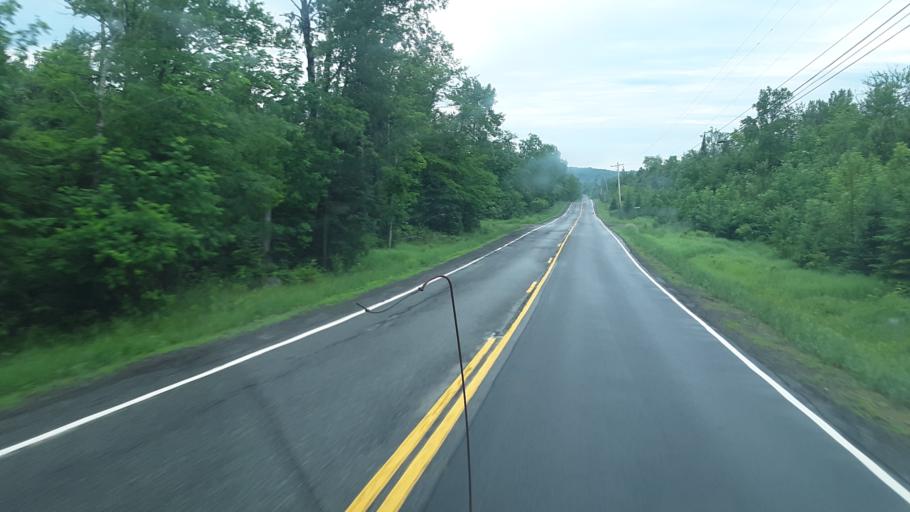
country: US
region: Maine
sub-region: Penobscot County
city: Patten
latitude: 46.1096
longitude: -68.4130
